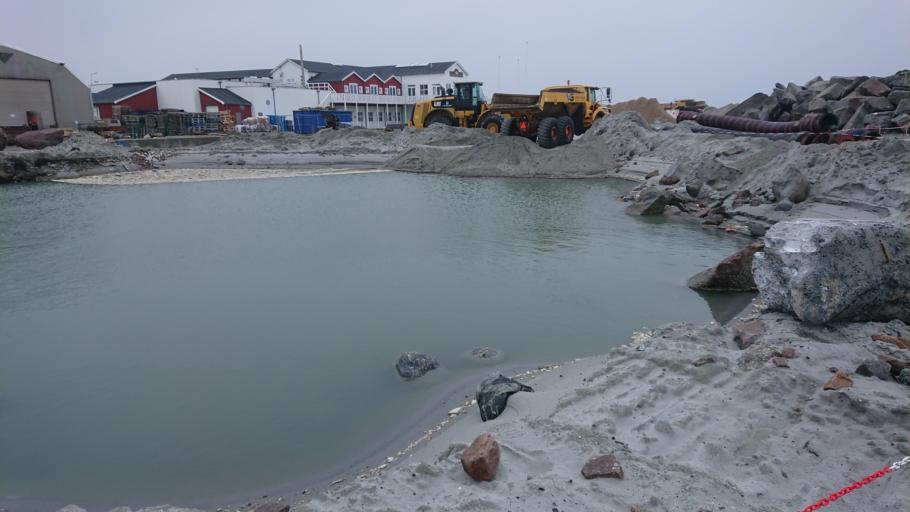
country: DK
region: North Denmark
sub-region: Frederikshavn Kommune
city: Skagen
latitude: 57.7198
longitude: 10.6051
